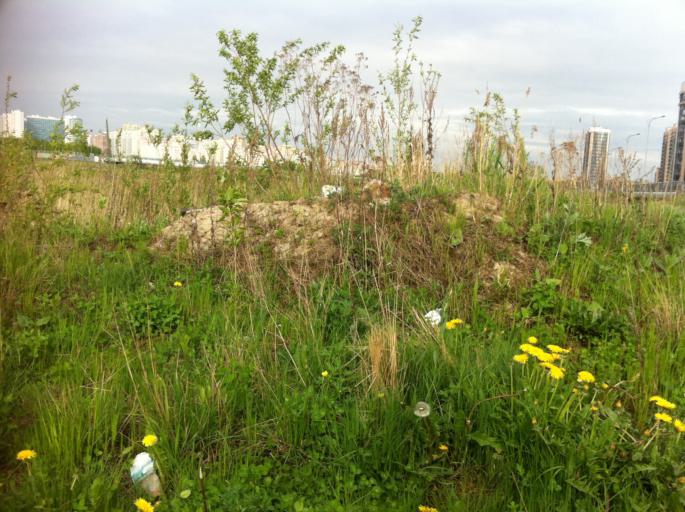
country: RU
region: St.-Petersburg
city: Sosnovaya Polyana
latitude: 59.8546
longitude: 30.1426
